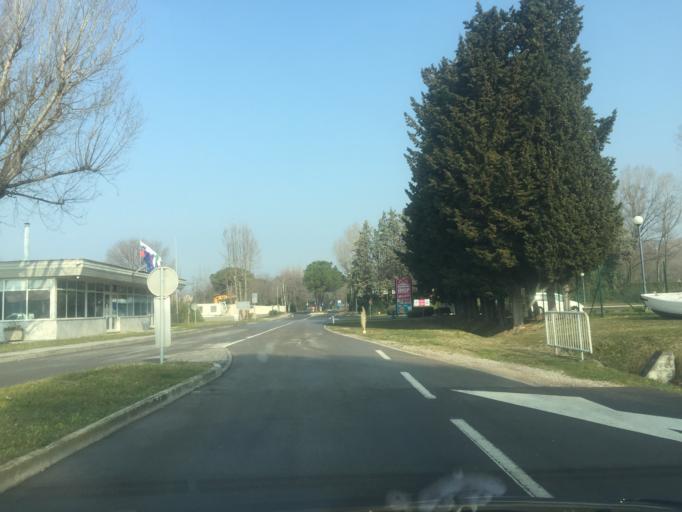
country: SI
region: Koper-Capodistria
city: Ankaran
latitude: 45.5940
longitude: 13.7241
